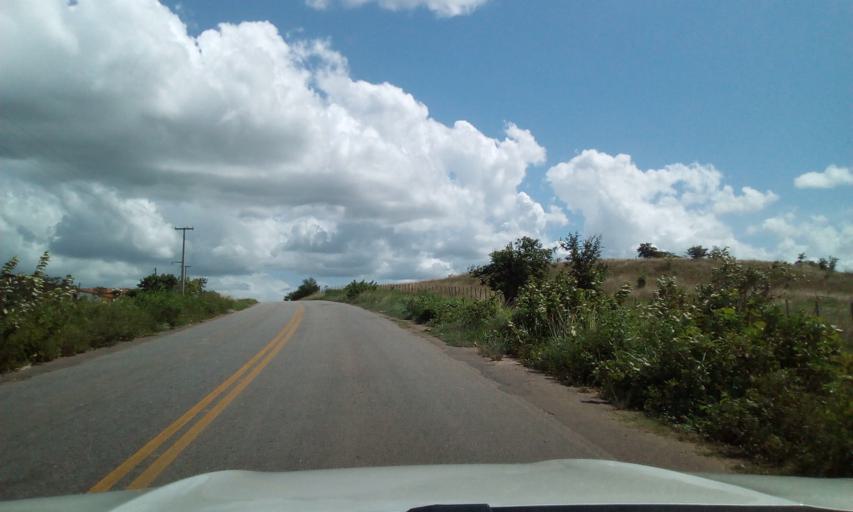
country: BR
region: Paraiba
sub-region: Guarabira
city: Guarabira
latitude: -6.8499
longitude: -35.3931
